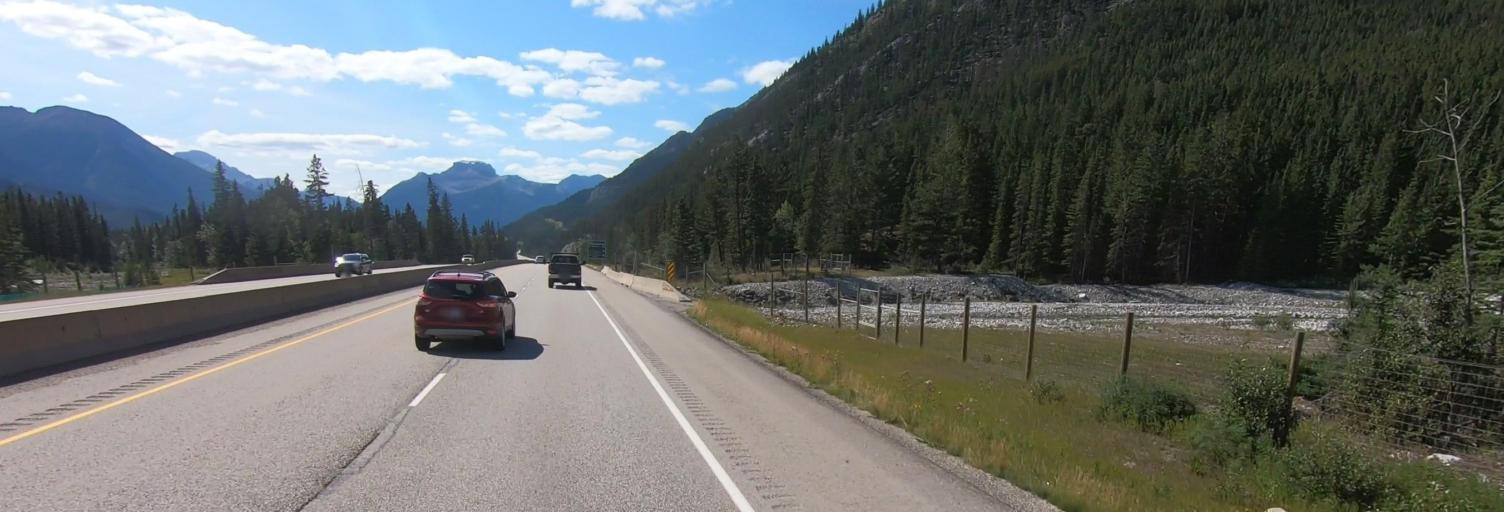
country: CA
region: Alberta
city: Banff
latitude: 51.1947
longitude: -115.5598
